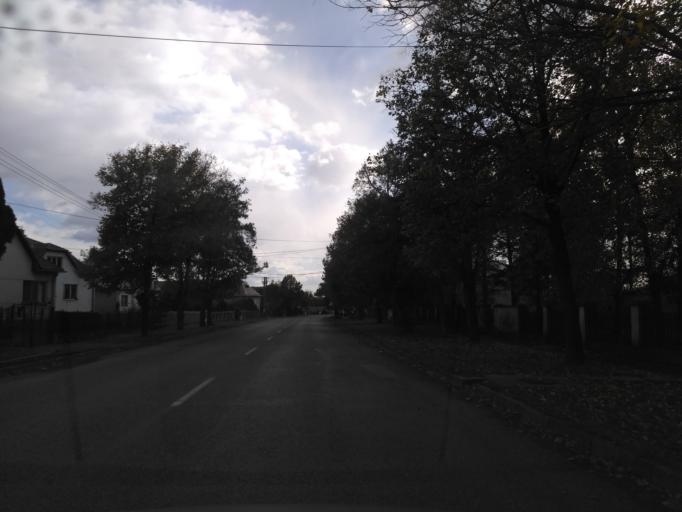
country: SK
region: Kosicky
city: Trebisov
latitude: 48.6517
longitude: 21.6771
